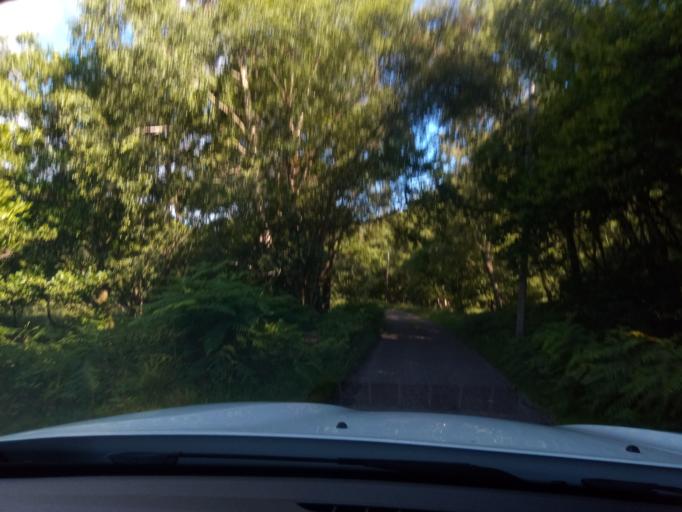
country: GB
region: Scotland
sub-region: Argyll and Bute
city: Isle Of Mull
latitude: 56.7645
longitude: -5.8205
